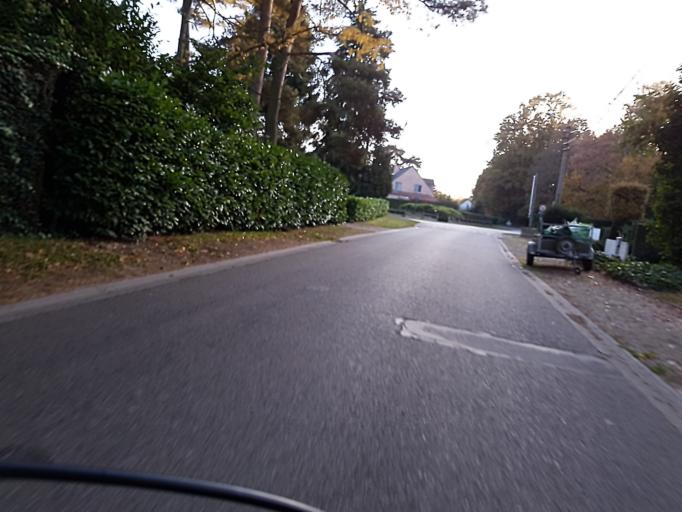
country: BE
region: Flanders
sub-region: Provincie Antwerpen
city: Bonheiden
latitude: 51.0246
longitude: 4.5316
